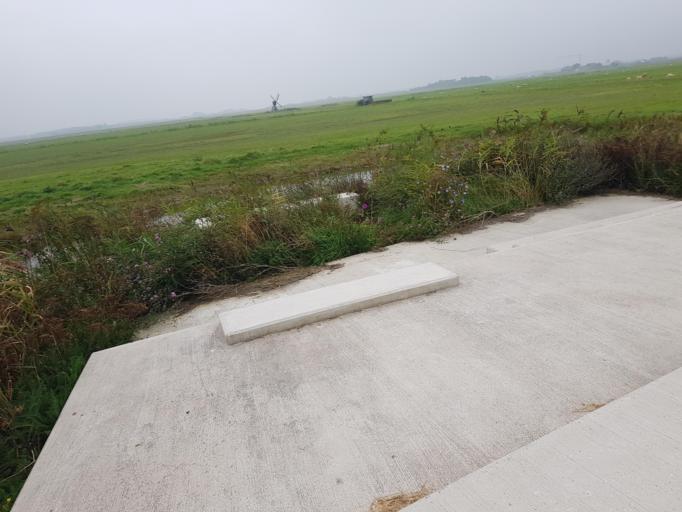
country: NL
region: North Holland
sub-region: Gemeente Texel
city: Den Burg
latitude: 53.0831
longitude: 4.7994
